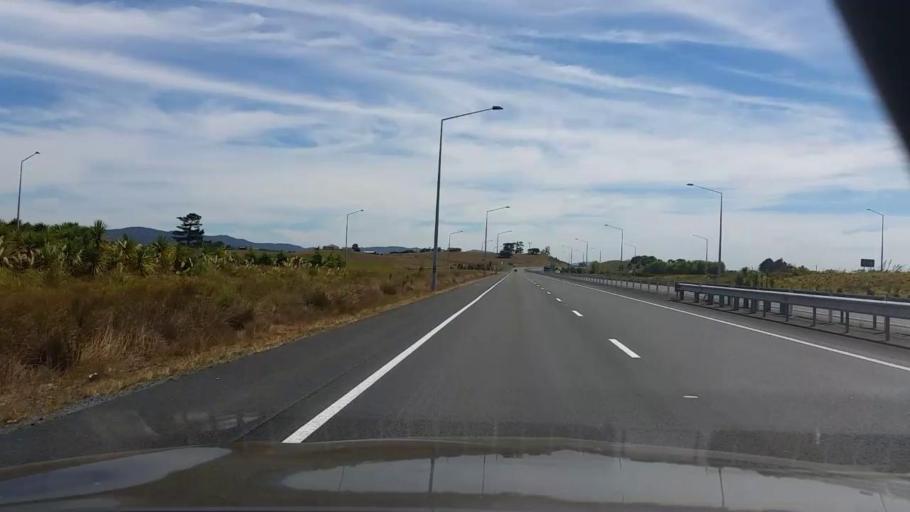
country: NZ
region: Waikato
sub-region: Waikato District
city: Ngaruawahia
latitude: -37.7324
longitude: 175.2097
